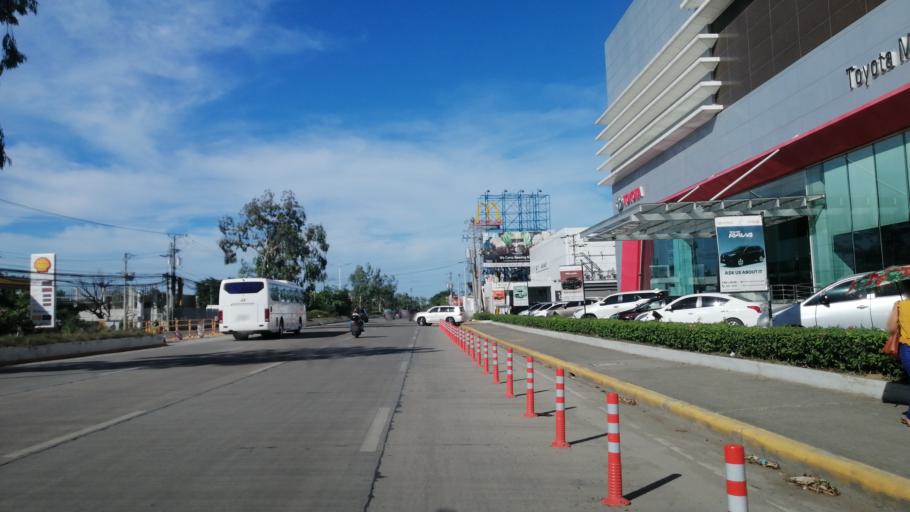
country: PH
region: Central Visayas
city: Mandaue City
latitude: 10.3208
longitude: 123.9320
